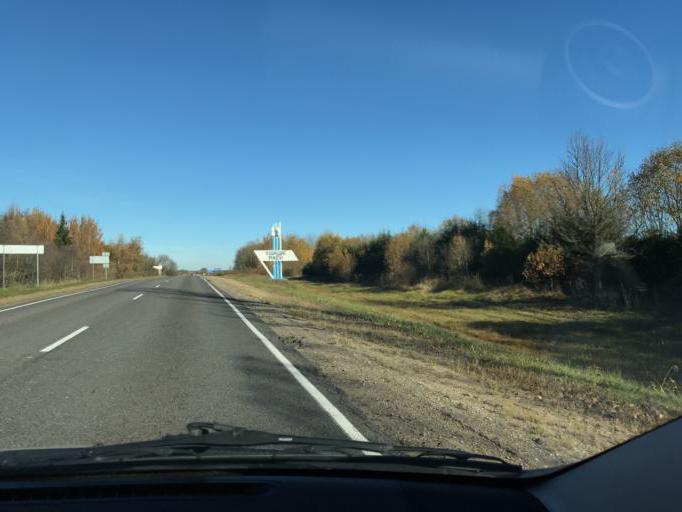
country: BY
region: Vitebsk
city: Lyepyel'
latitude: 55.0373
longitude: 28.7484
